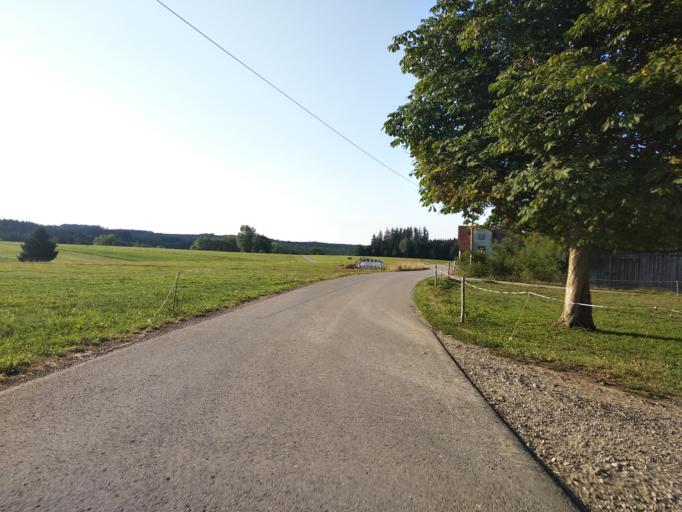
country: DE
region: Bavaria
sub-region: Swabia
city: Legau
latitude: 47.8679
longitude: 10.1151
